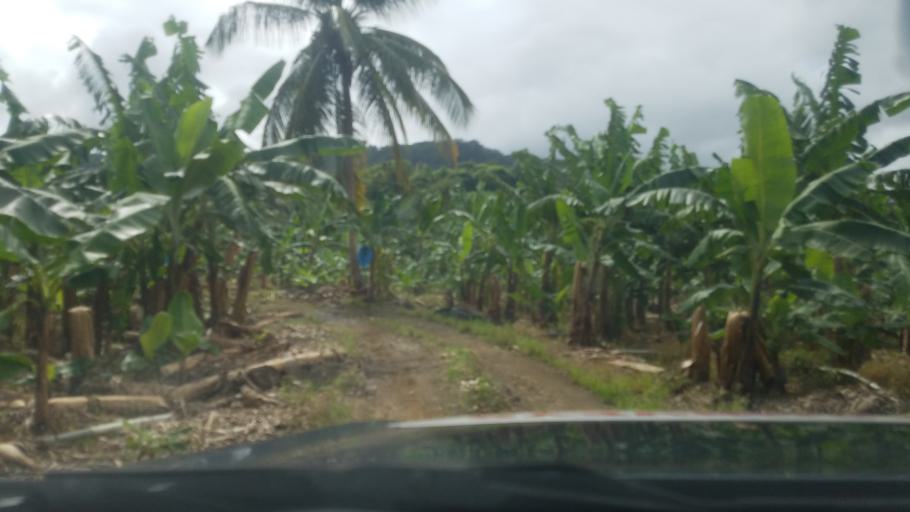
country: LC
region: Dennery Quarter
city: Dennery
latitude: 13.9322
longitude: -60.9250
